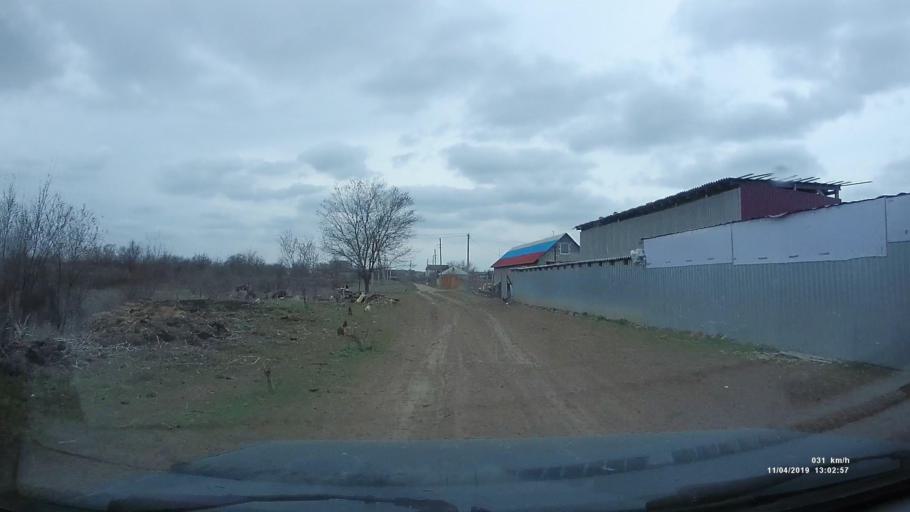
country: RU
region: Rostov
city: Staraya Stanitsa
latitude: 48.2881
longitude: 40.3541
